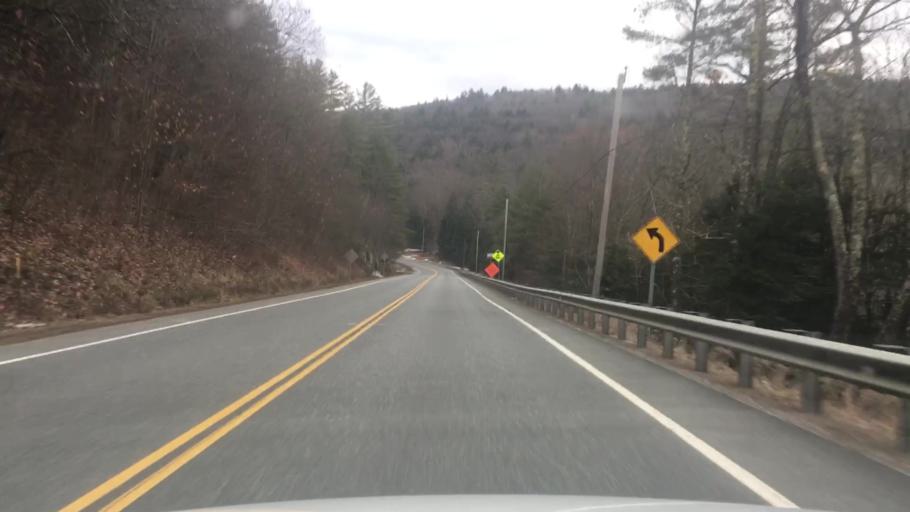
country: US
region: New Hampshire
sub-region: Cheshire County
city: Westmoreland
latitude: 42.9914
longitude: -72.4310
